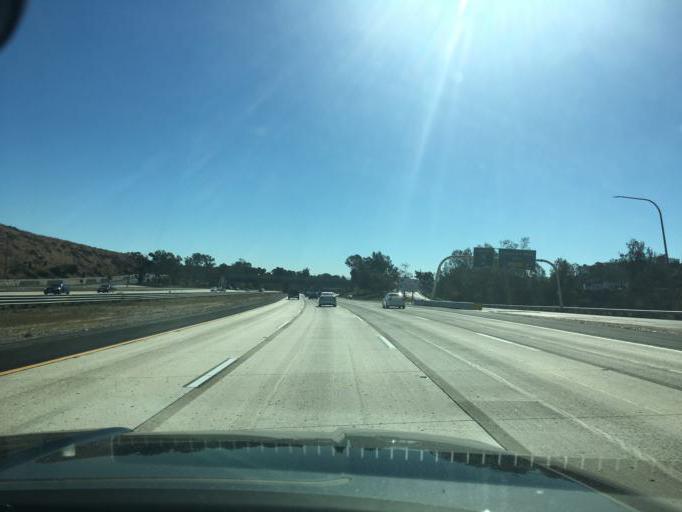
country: US
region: California
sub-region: San Diego County
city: La Mesa
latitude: 32.8372
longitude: -117.1207
